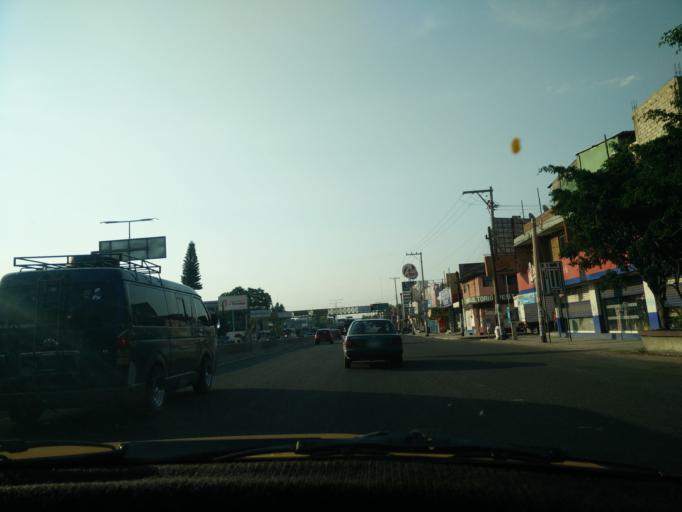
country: MX
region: Oaxaca
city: Oaxaca de Juarez
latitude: 17.0818
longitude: -96.7432
